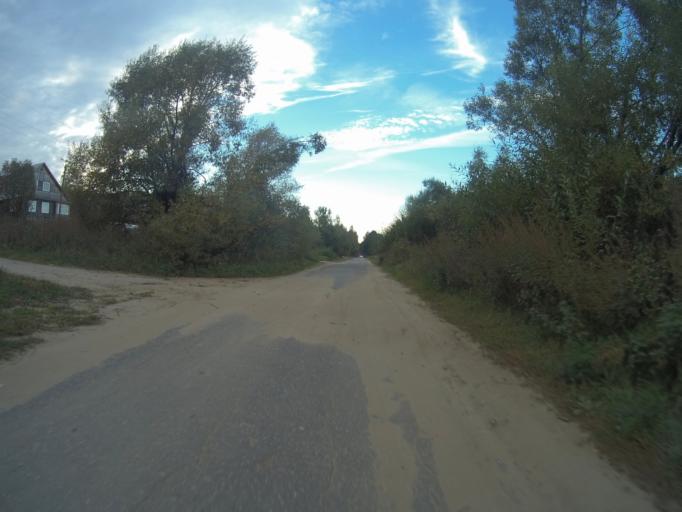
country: RU
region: Vladimir
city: Raduzhnyy
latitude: 56.0050
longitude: 40.3641
